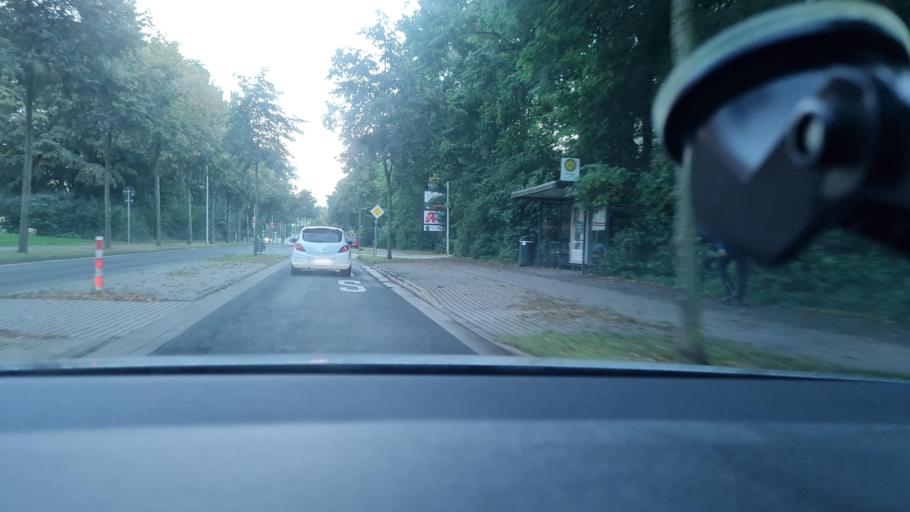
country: DE
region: North Rhine-Westphalia
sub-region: Regierungsbezirk Dusseldorf
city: Moers
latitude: 51.4855
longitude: 6.6170
